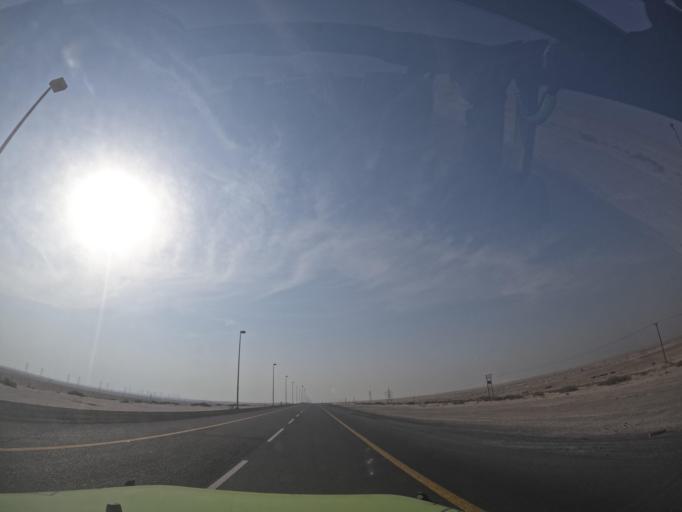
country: AE
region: Dubai
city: Dubai
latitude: 24.7601
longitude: 55.0985
